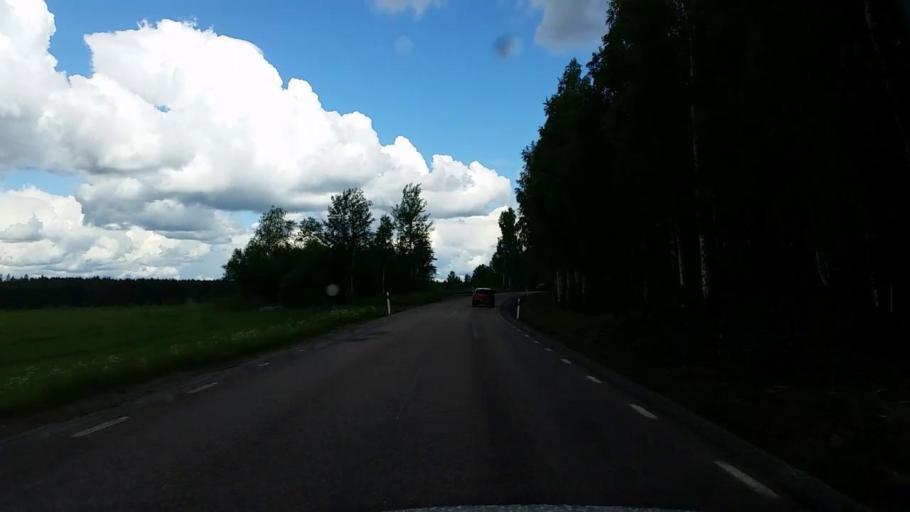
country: SE
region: Vaestmanland
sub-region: Skinnskattebergs Kommun
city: Skinnskatteberg
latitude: 59.8399
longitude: 15.8410
